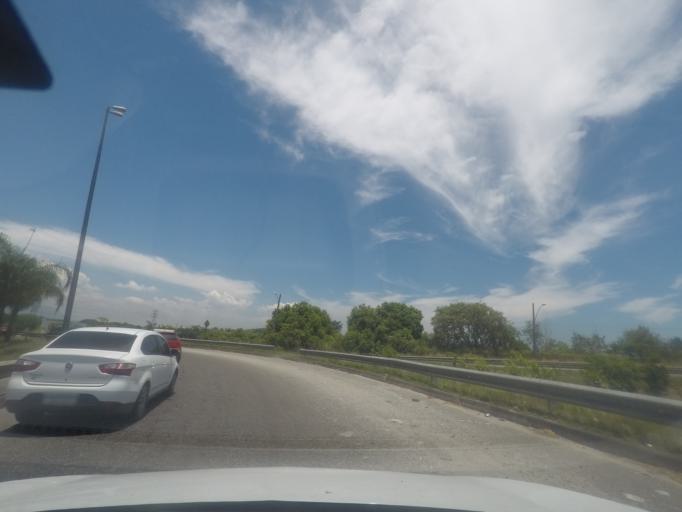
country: BR
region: Rio de Janeiro
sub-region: Itaguai
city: Itaguai
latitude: -22.8957
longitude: -43.6806
